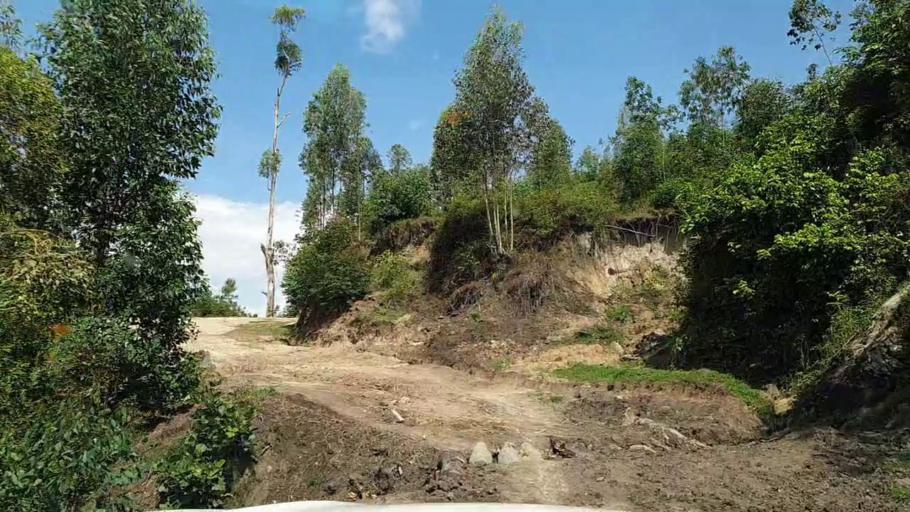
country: RW
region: Southern Province
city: Gikongoro
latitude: -2.3634
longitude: 29.5342
